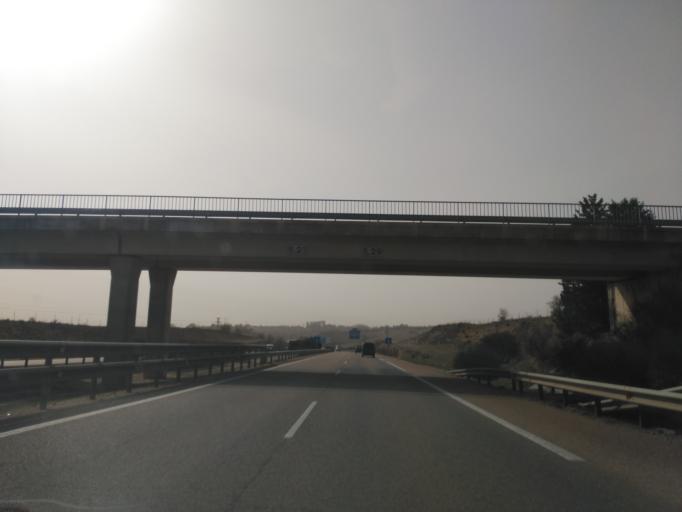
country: ES
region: Castille and Leon
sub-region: Provincia de Valladolid
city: Santovenia de Pisuerga
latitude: 41.6928
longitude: -4.7239
